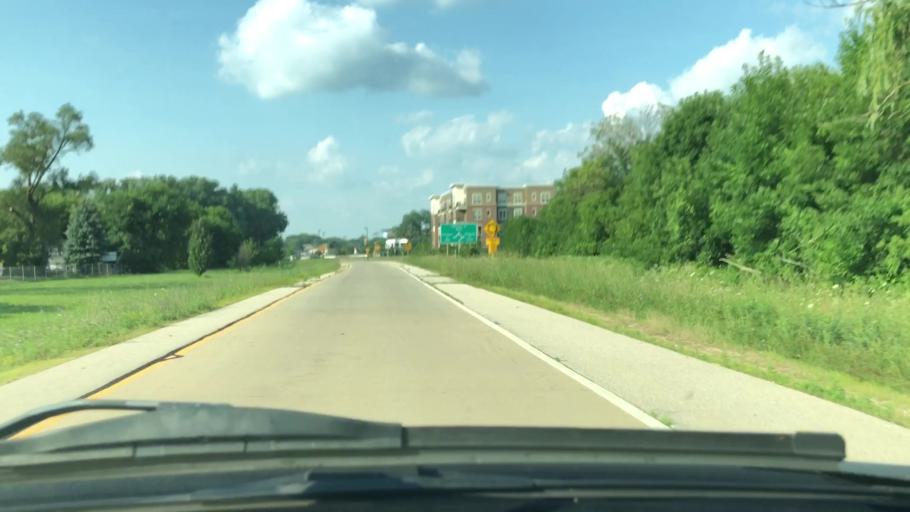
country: US
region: Wisconsin
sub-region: Dane County
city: Middleton
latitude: 43.1001
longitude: -89.5136
